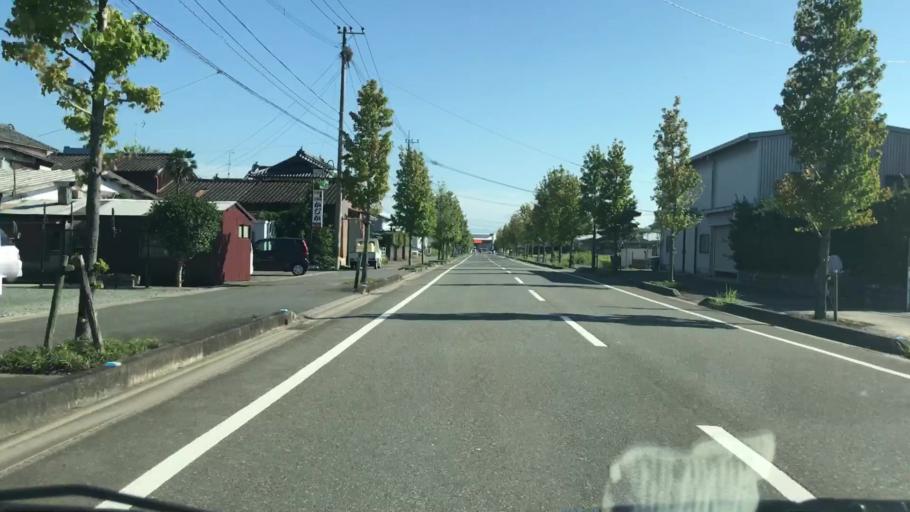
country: JP
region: Saga Prefecture
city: Okawa
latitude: 33.1848
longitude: 130.3138
